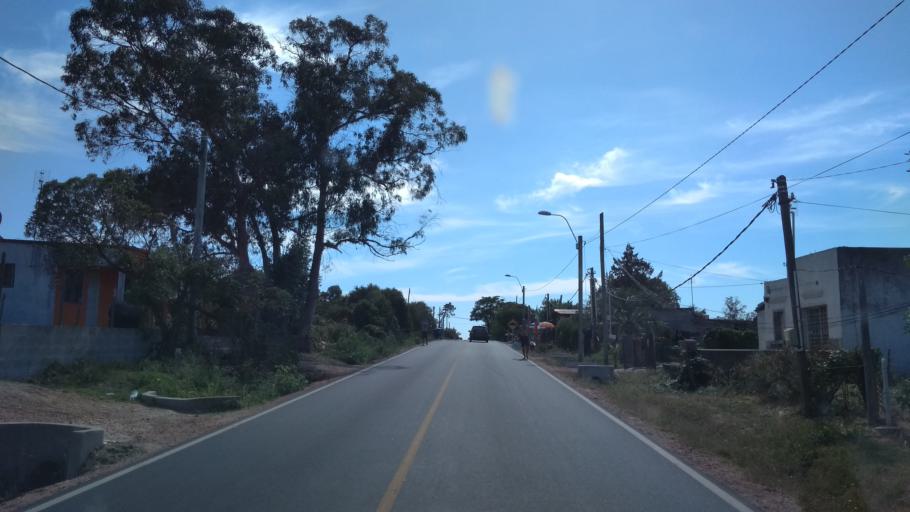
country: UY
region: Canelones
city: Joaquin Suarez
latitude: -34.7301
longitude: -56.0313
